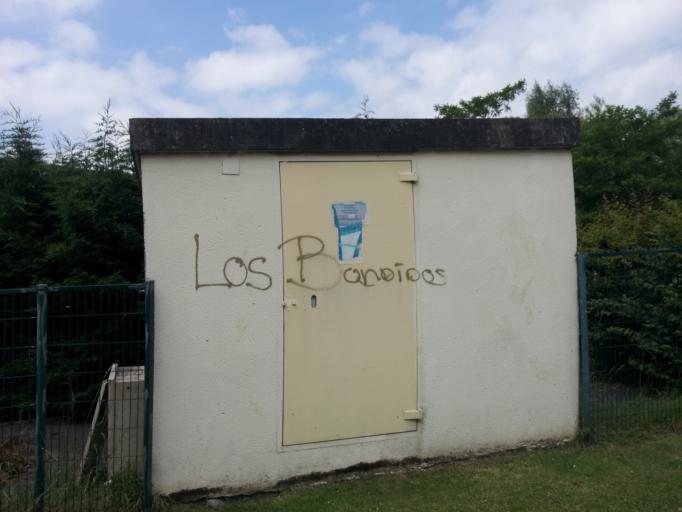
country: FR
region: Ile-de-France
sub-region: Departement de l'Essonne
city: Bondoufle
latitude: 48.6055
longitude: 2.3723
